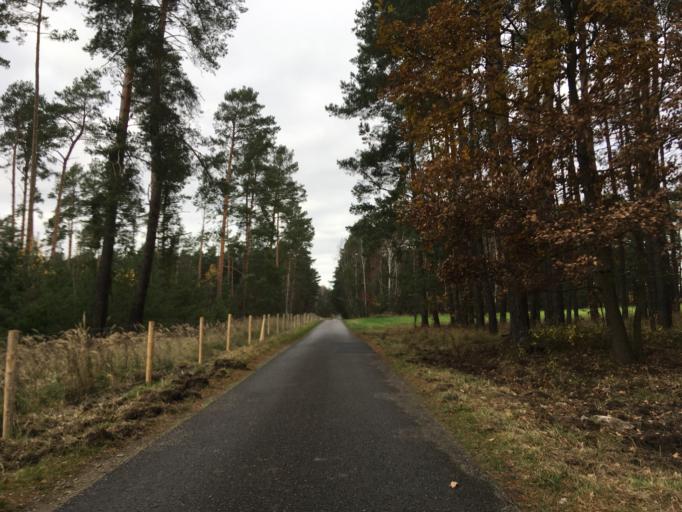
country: DE
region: Brandenburg
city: Jamlitz
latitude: 52.0228
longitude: 14.4762
